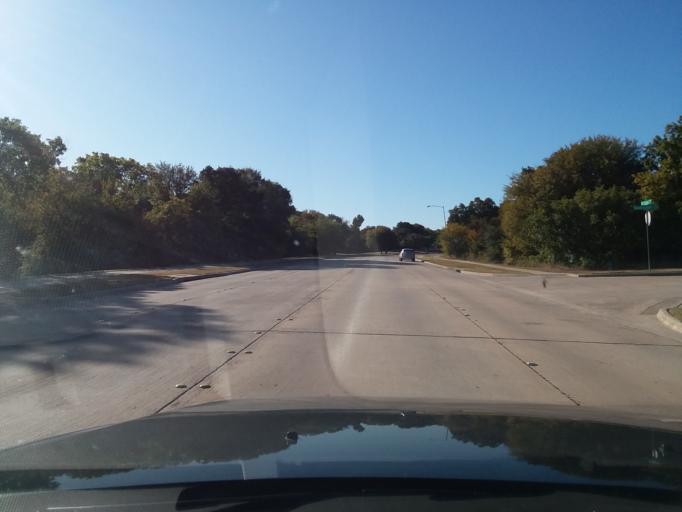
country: US
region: Texas
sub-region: Denton County
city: Lewisville
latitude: 33.0185
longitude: -97.0277
